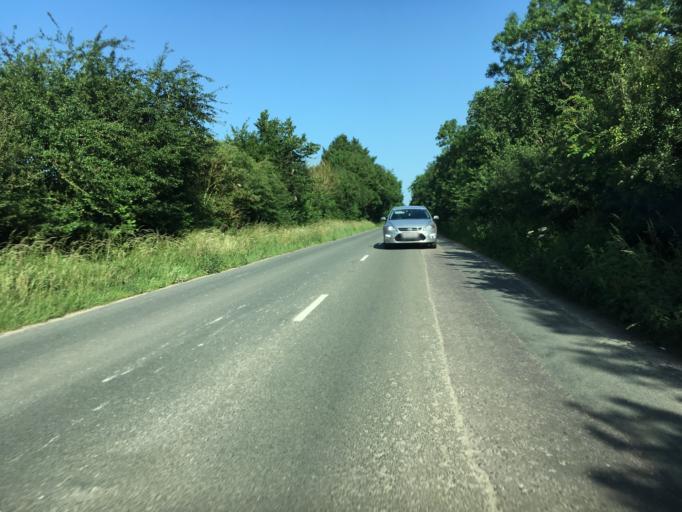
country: GB
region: England
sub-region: Oxfordshire
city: Bicester
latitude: 51.9042
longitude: -1.1981
